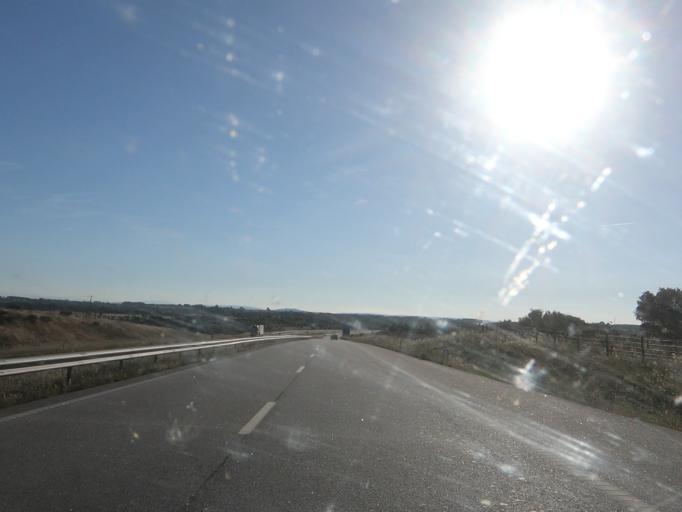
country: ES
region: Castille and Leon
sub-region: Provincia de Salamanca
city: Fuentes de Onoro
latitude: 40.6044
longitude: -6.9598
